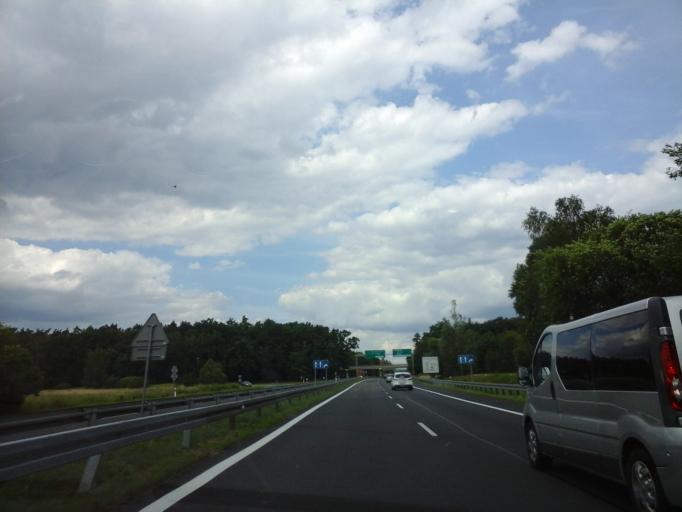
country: PL
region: West Pomeranian Voivodeship
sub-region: Powiat goleniowski
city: Goleniow
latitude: 53.5678
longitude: 14.7976
